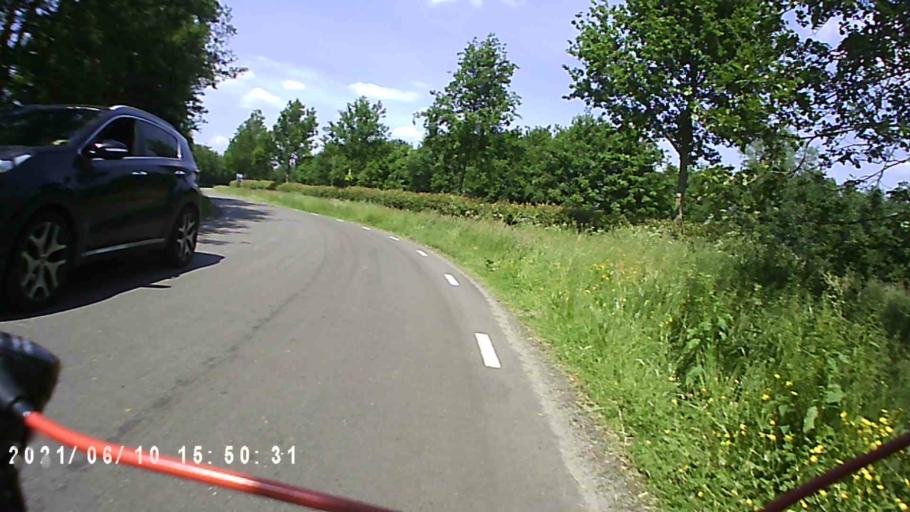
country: NL
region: Friesland
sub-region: Gemeente Achtkarspelen
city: Harkema
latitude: 53.1696
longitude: 6.1185
